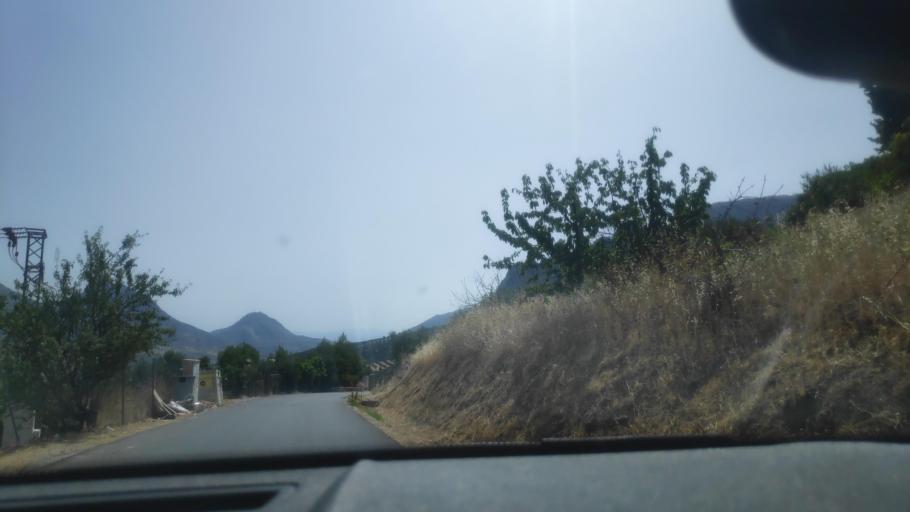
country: ES
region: Andalusia
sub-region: Provincia de Jaen
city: Torres
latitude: 37.7924
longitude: -3.4635
